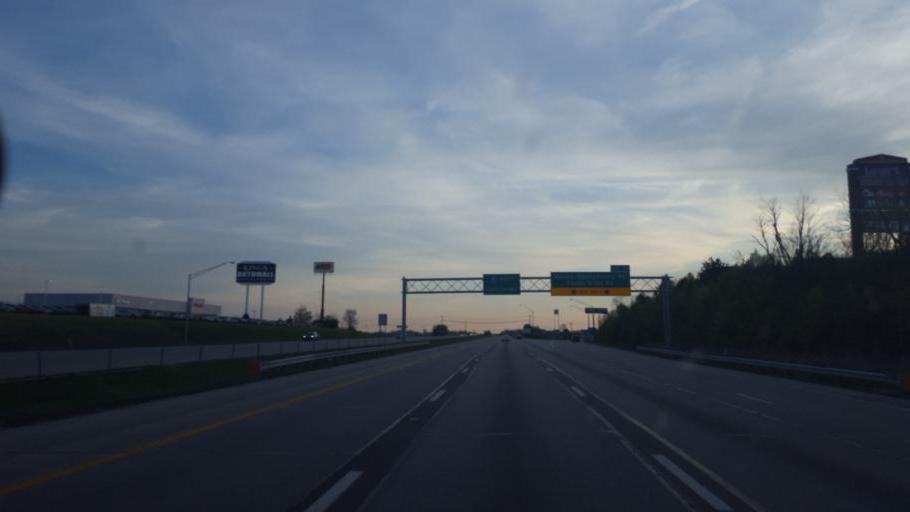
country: US
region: Ohio
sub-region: Hamilton County
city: Sixteen Mile Stand
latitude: 39.2976
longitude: -84.3108
